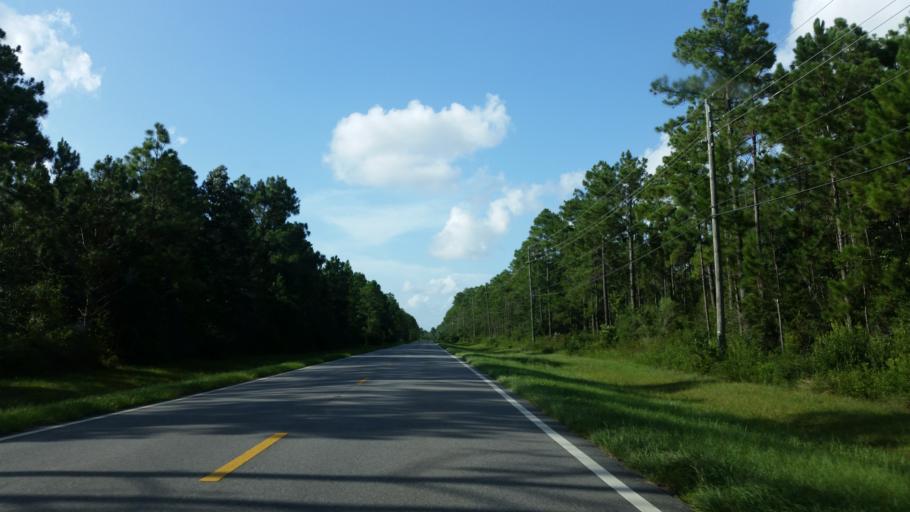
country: US
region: Florida
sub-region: Santa Rosa County
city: Bagdad
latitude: 30.5202
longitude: -87.0539
